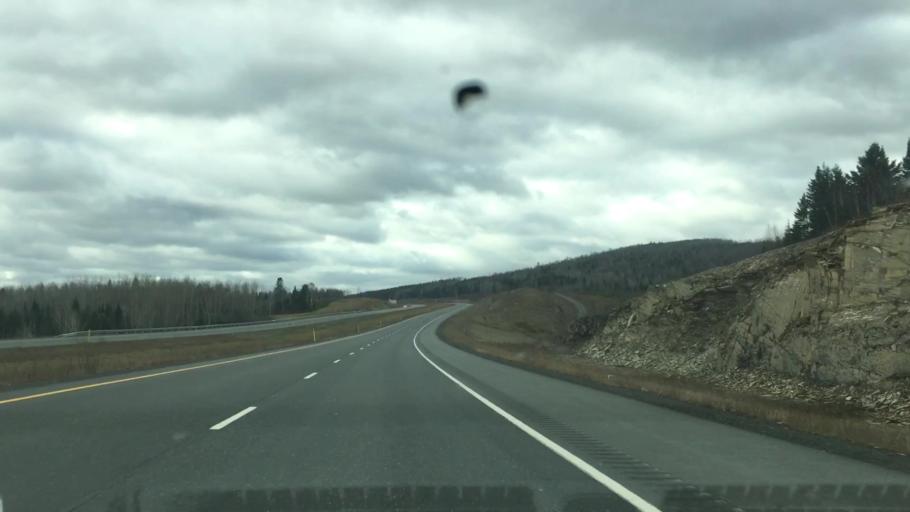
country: US
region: Maine
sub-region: Aroostook County
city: Fort Fairfield
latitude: 46.7343
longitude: -67.7206
